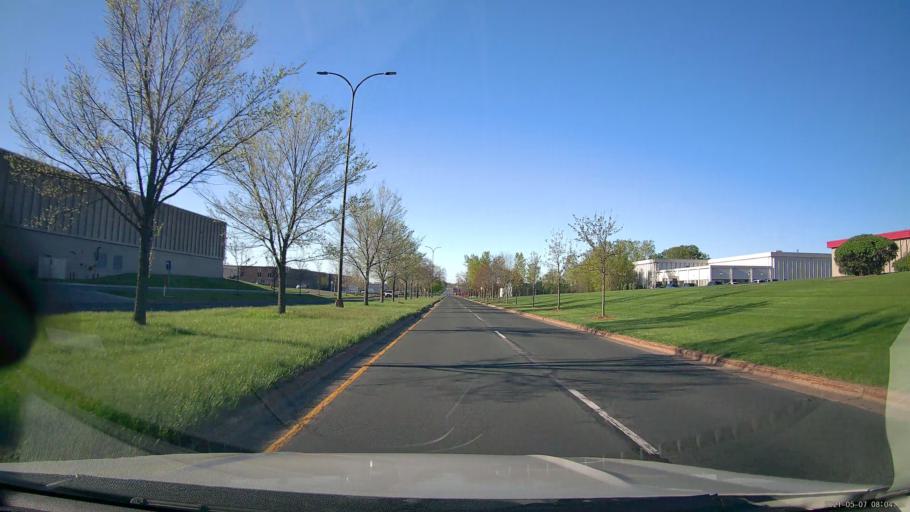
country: US
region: Minnesota
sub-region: Ramsey County
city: Lauderdale
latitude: 44.9976
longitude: -93.2117
